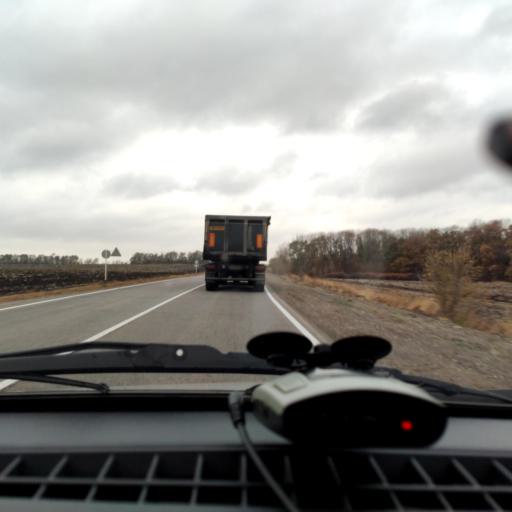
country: RU
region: Voronezj
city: Shilovo
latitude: 51.4546
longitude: 38.9738
